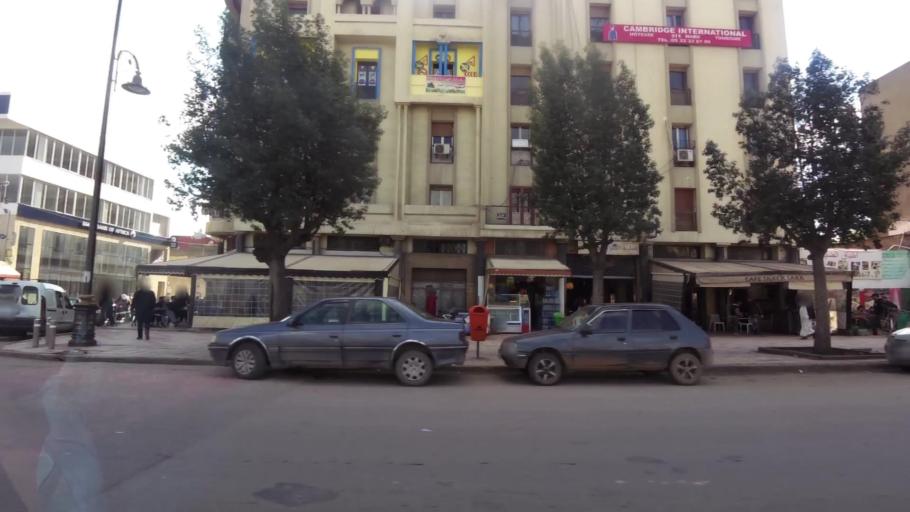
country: MA
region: Chaouia-Ouardigha
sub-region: Settat Province
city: Berrechid
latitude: 33.2665
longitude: -7.5838
